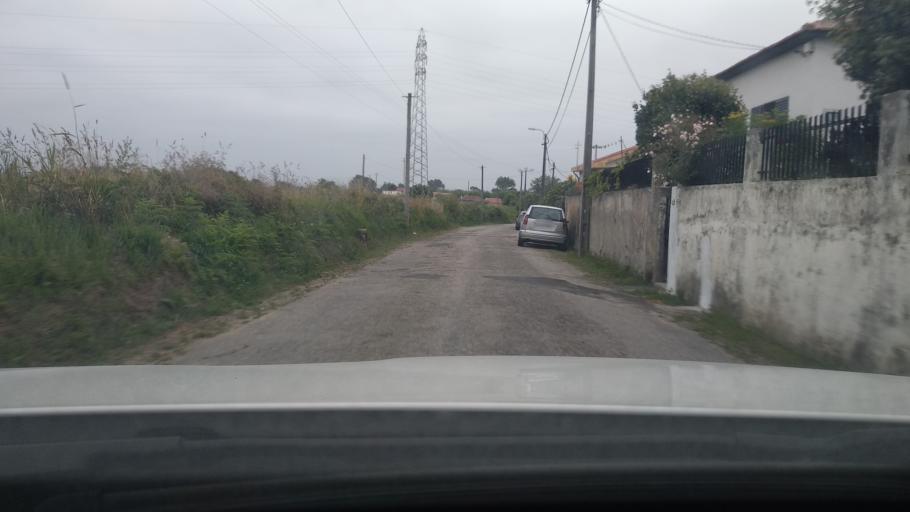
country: PT
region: Aveiro
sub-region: Espinho
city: Silvalde
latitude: 40.9872
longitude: -8.6332
